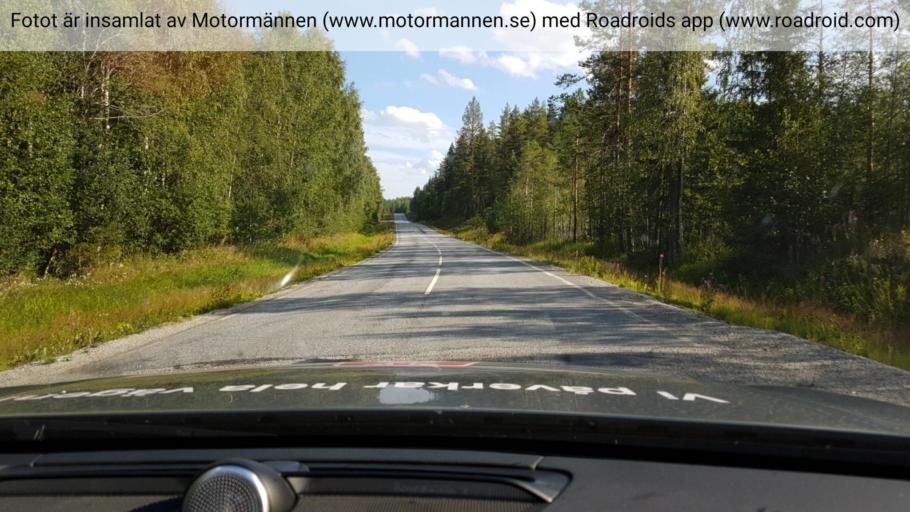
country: SE
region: Vaesterbotten
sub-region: Dorotea Kommun
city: Dorotea
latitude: 63.8963
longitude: 16.3609
